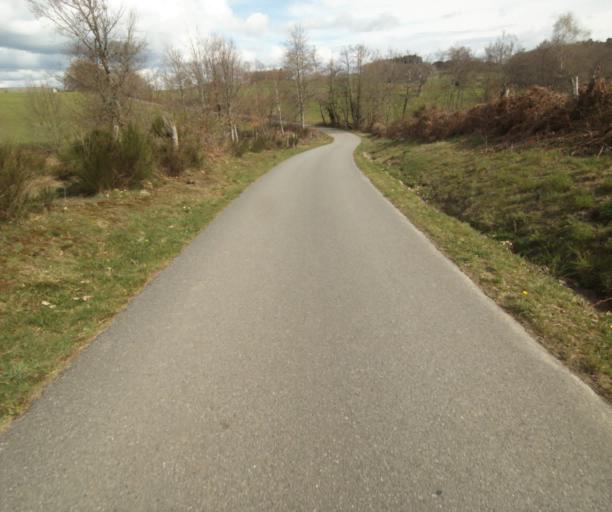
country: FR
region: Limousin
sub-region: Departement de la Correze
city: Correze
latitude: 45.3628
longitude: 1.8986
